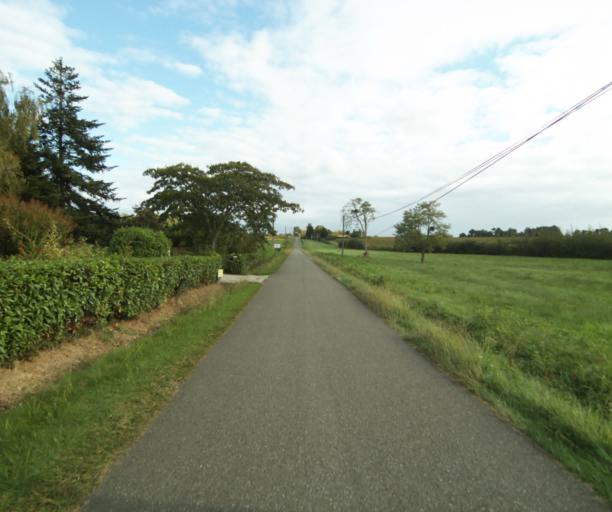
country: FR
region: Midi-Pyrenees
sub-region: Departement du Gers
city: Eauze
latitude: 43.8866
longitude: 0.0719
